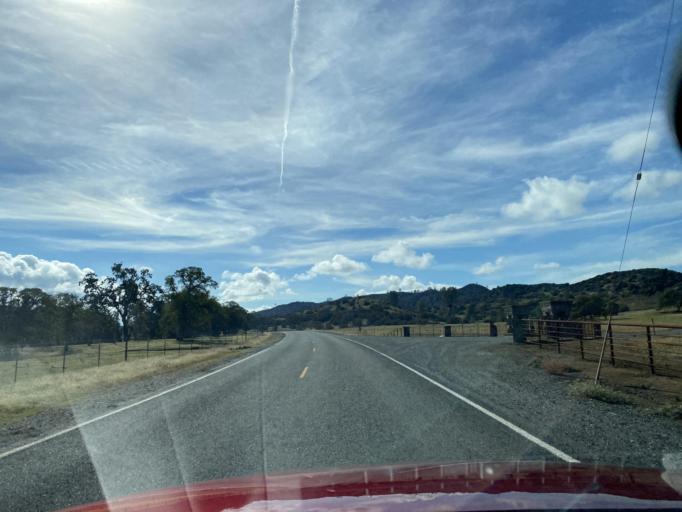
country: US
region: California
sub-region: Glenn County
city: Willows
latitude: 39.4562
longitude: -122.5140
